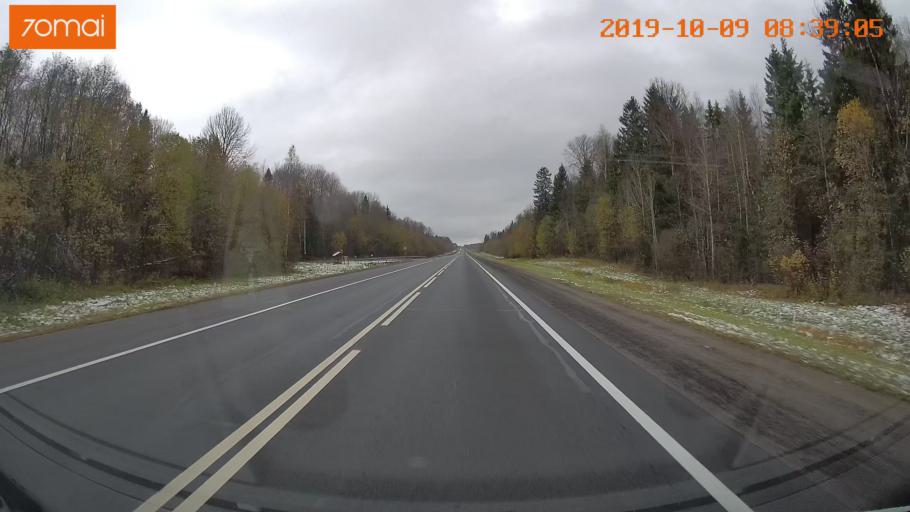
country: RU
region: Vologda
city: Gryazovets
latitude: 58.9661
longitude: 40.1576
